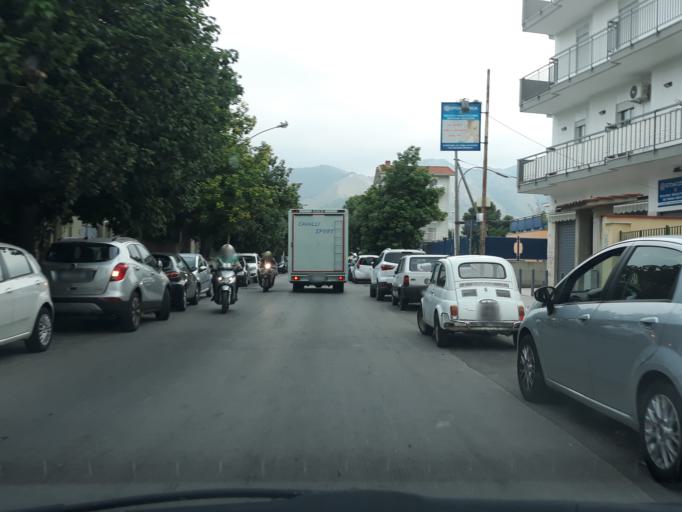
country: IT
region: Sicily
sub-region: Palermo
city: Monreale
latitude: 38.0947
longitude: 13.3194
